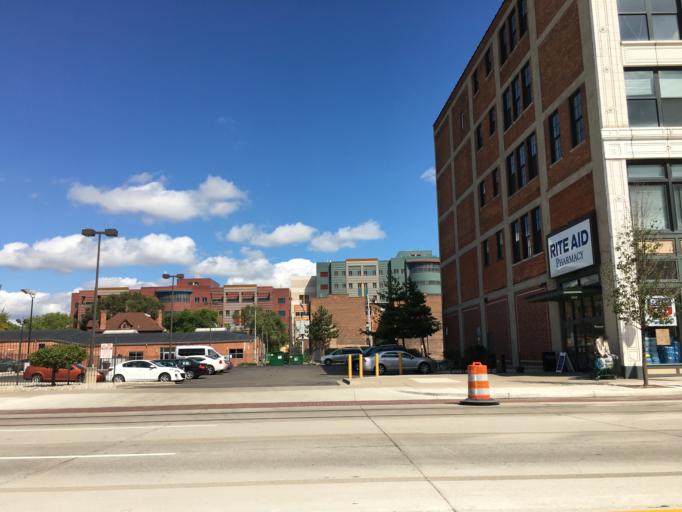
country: US
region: Michigan
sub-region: Wayne County
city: Detroit
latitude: 42.3541
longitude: -83.0626
